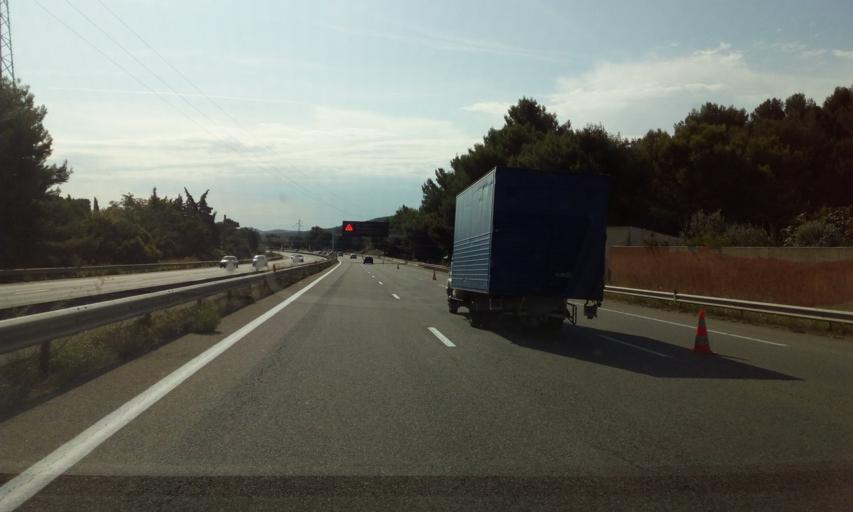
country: FR
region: Provence-Alpes-Cote d'Azur
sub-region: Departement du Var
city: Sanary-sur-Mer
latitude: 43.1319
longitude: 5.8134
